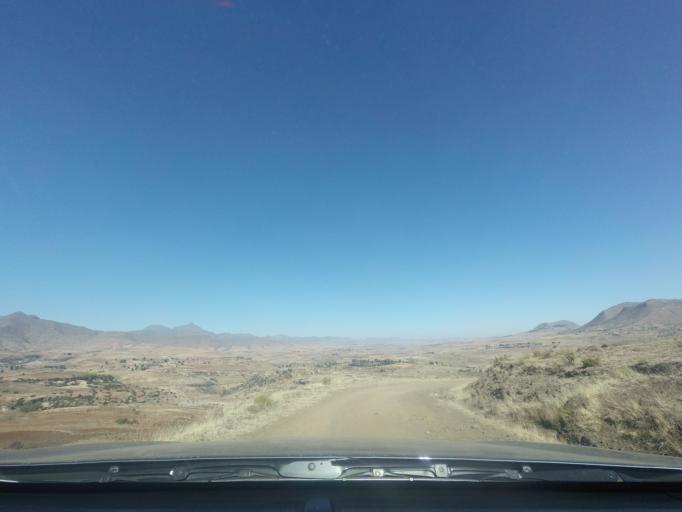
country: LS
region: Berea
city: Teyateyaneng
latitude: -29.2397
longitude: 27.8717
